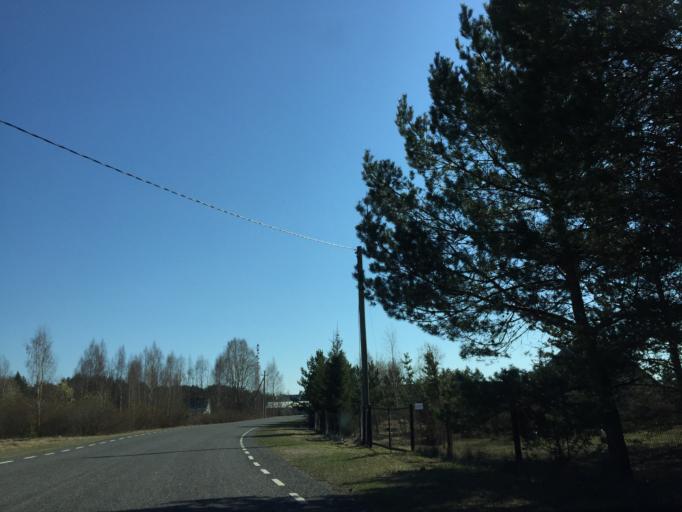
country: EE
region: Ida-Virumaa
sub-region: Johvi vald
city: Johvi
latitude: 59.0129
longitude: 27.4341
